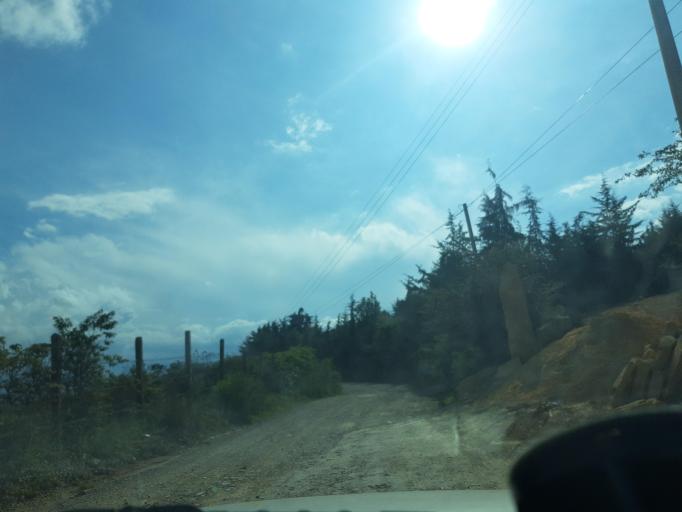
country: CO
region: Boyaca
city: Villa de Leiva
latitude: 5.6540
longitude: -73.5358
